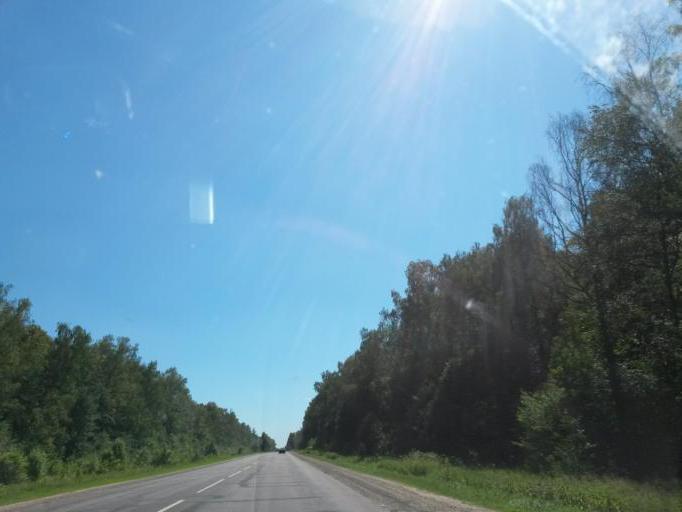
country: RU
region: Moskovskaya
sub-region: Chekhovskiy Rayon
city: Chekhov
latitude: 55.0857
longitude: 37.4411
